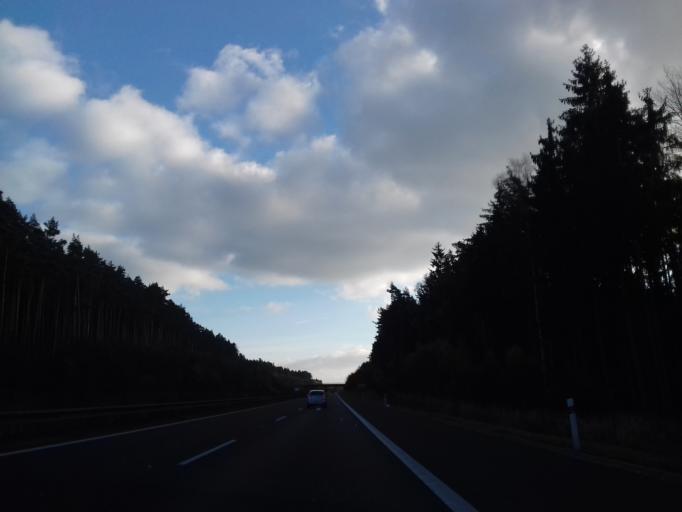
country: CZ
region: Plzensky
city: Line
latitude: 49.6942
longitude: 13.2952
